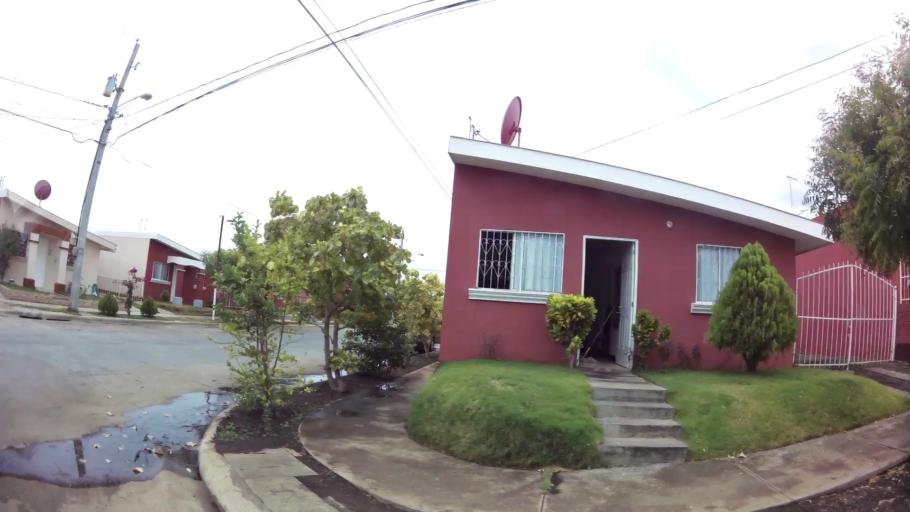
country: NI
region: Managua
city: Managua
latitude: 12.1219
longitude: -86.1811
